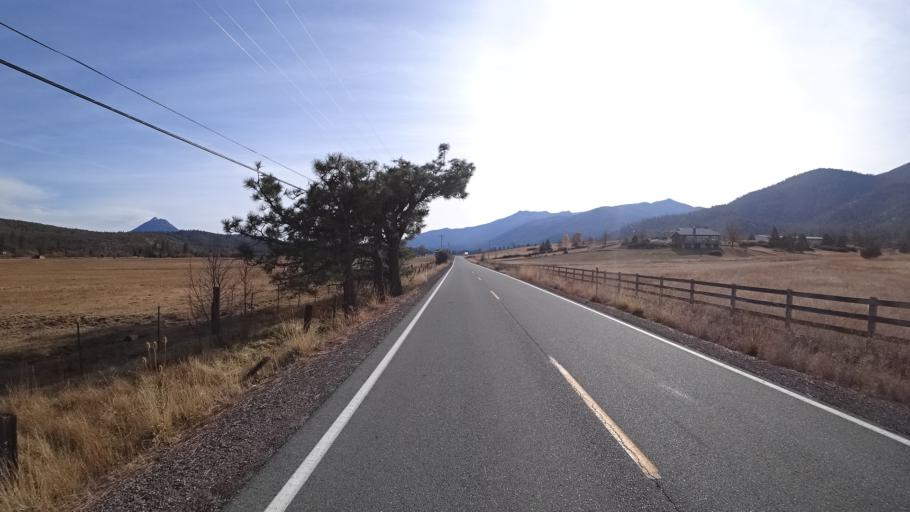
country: US
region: California
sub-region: Siskiyou County
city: Weed
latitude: 41.4286
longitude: -122.4373
